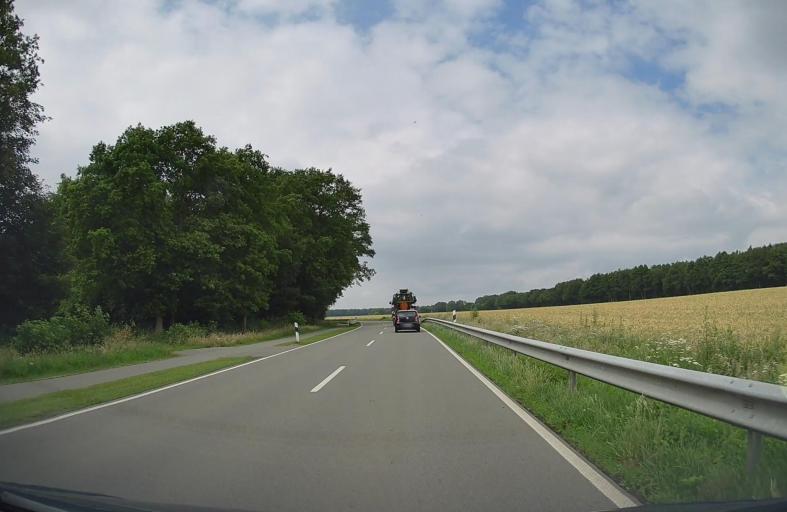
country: DE
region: Lower Saxony
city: Friesoythe
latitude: 53.0477
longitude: 7.8226
